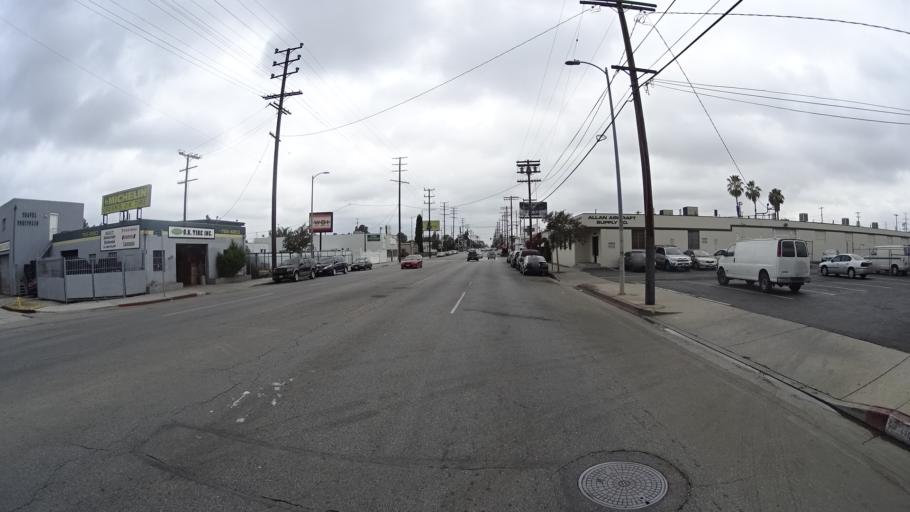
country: US
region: California
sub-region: Los Angeles County
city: North Hollywood
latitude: 34.1940
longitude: -118.3859
